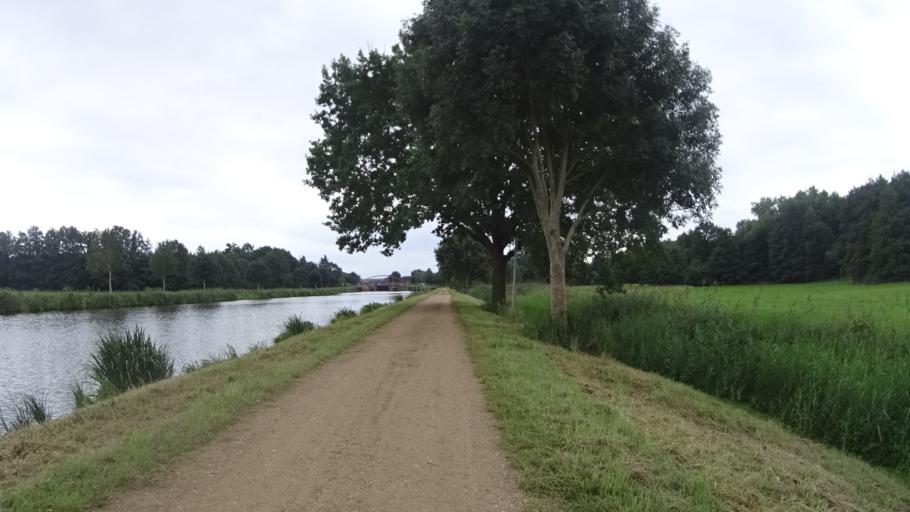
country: DE
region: Schleswig-Holstein
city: Kuhsen
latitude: 53.6777
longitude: 10.6356
